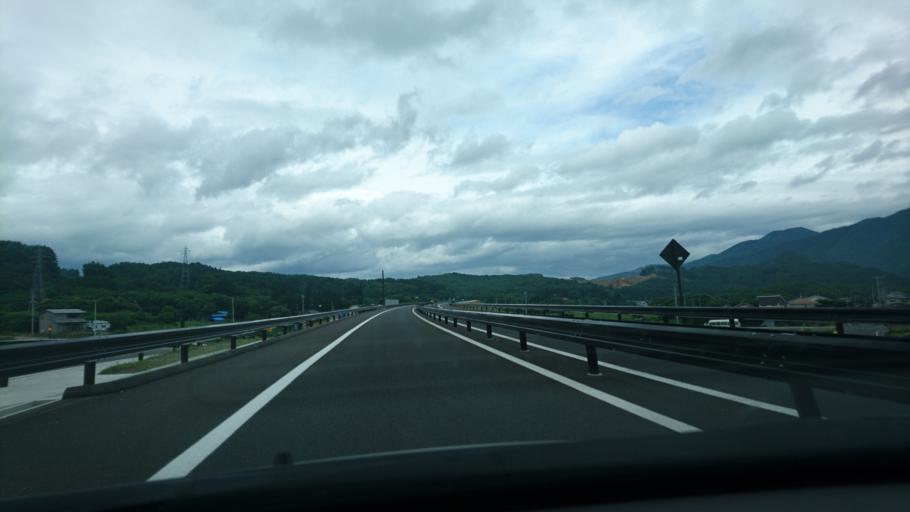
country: JP
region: Iwate
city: Yamada
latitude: 39.5391
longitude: 141.9198
